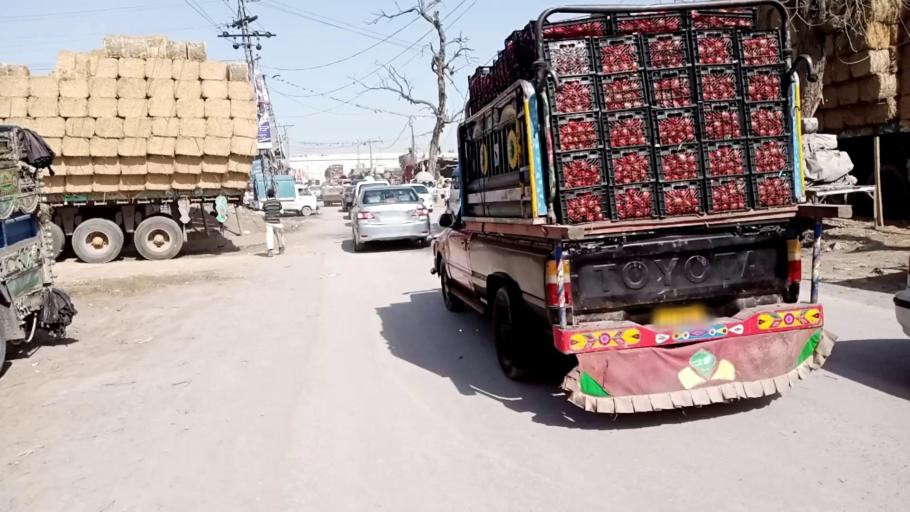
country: PK
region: Khyber Pakhtunkhwa
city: Peshawar
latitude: 34.0180
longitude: 71.6467
